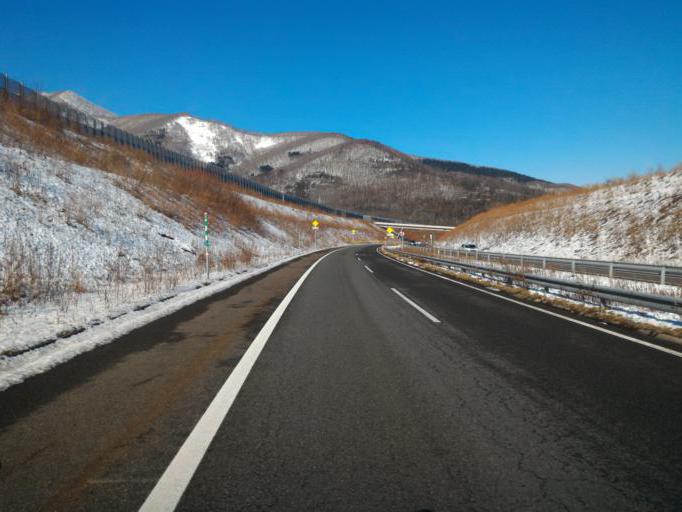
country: JP
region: Hokkaido
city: Otofuke
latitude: 43.0371
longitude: 142.7861
